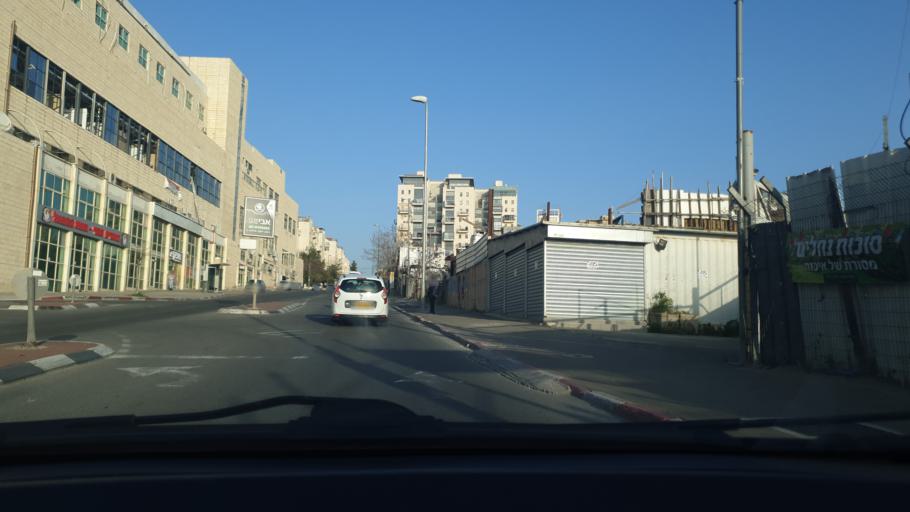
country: PS
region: West Bank
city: Bayt Iksa
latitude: 31.7932
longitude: 35.1879
